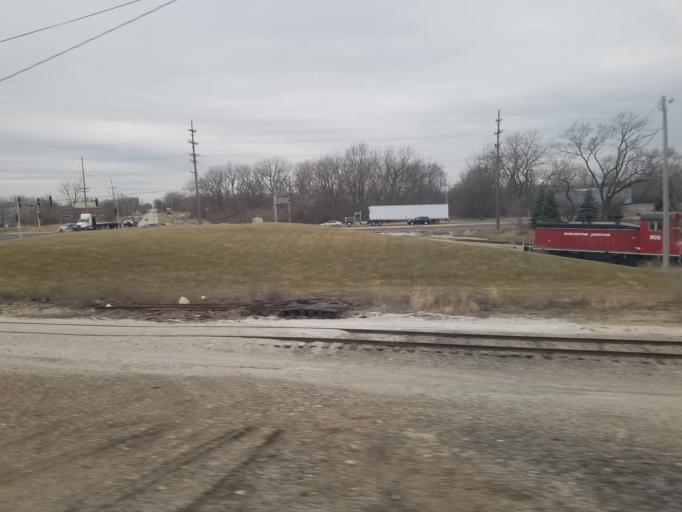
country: US
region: Illinois
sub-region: Kane County
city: Montgomery
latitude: 41.7305
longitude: -88.3420
